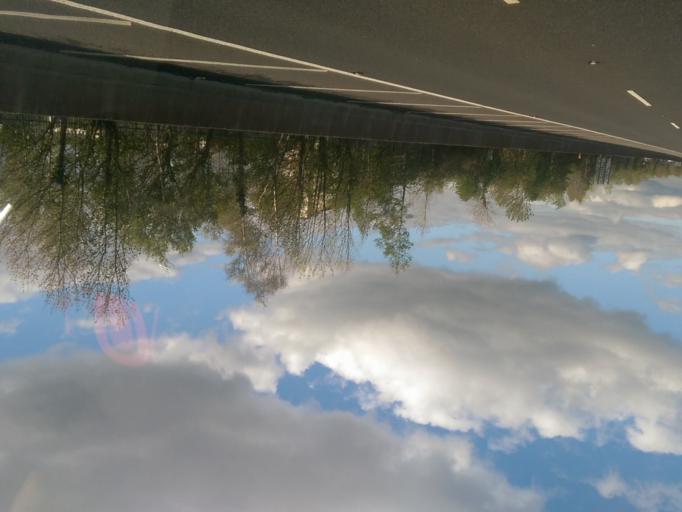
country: IE
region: Leinster
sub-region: An Iarmhi
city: Athlone
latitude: 53.4287
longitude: -7.9163
